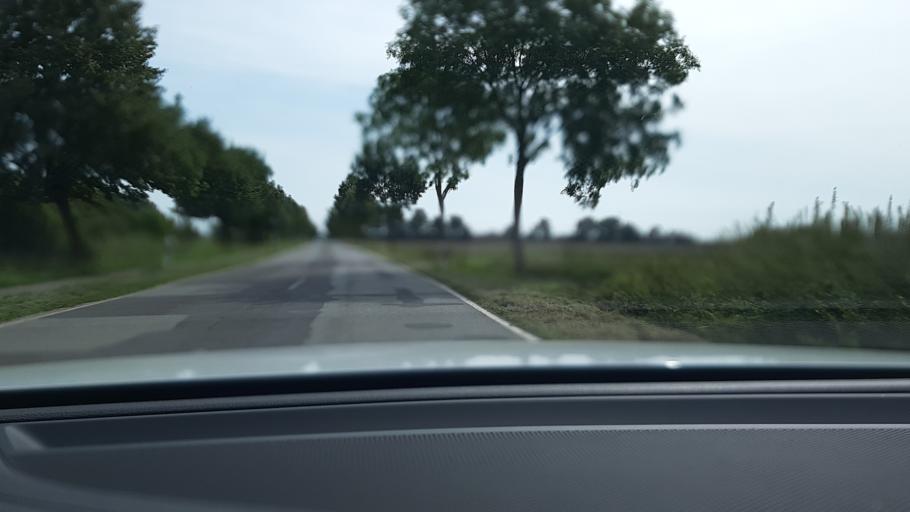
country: DE
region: Schleswig-Holstein
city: Heilshoop
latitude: 53.9047
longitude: 10.5235
